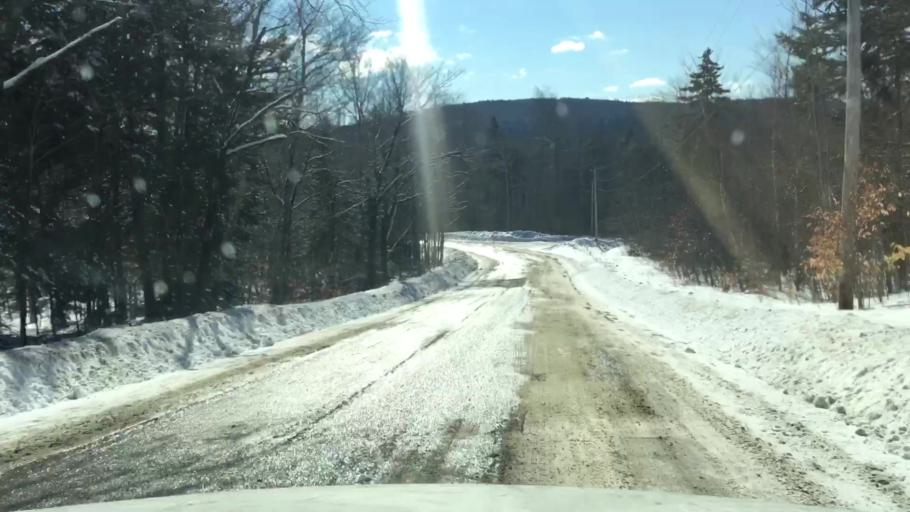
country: US
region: Maine
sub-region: Washington County
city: Calais
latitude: 45.0719
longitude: -67.4998
